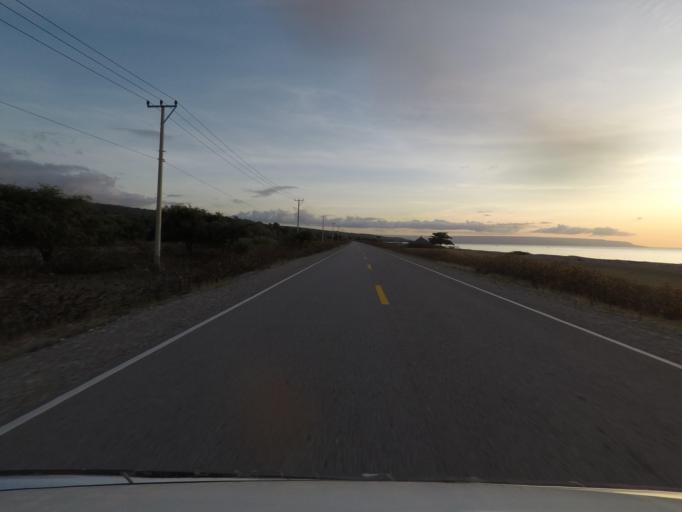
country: TL
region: Baucau
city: Baucau
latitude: -8.4436
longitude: 126.6499
